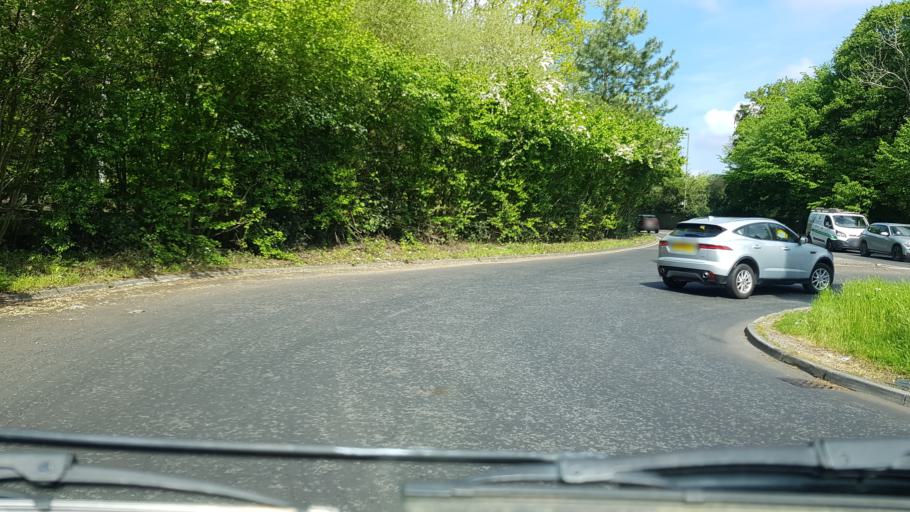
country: GB
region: England
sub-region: Surrey
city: Leatherhead
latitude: 51.3196
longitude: -0.3419
